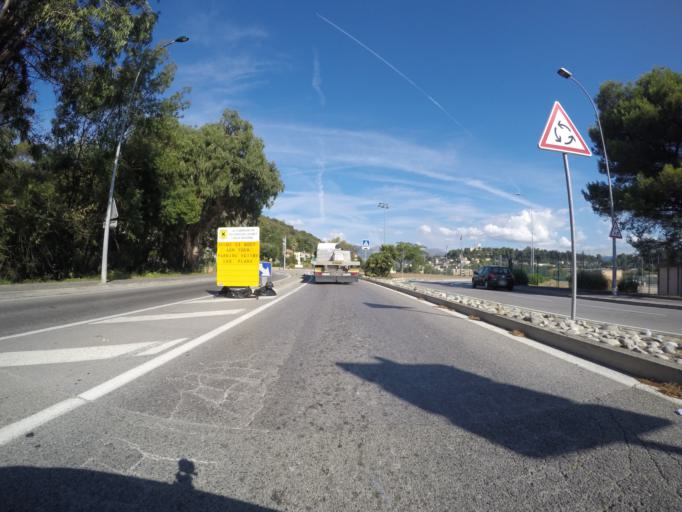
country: FR
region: Provence-Alpes-Cote d'Azur
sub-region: Departement des Alpes-Maritimes
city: Villeneuve-Loubet
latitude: 43.6519
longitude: 7.1285
